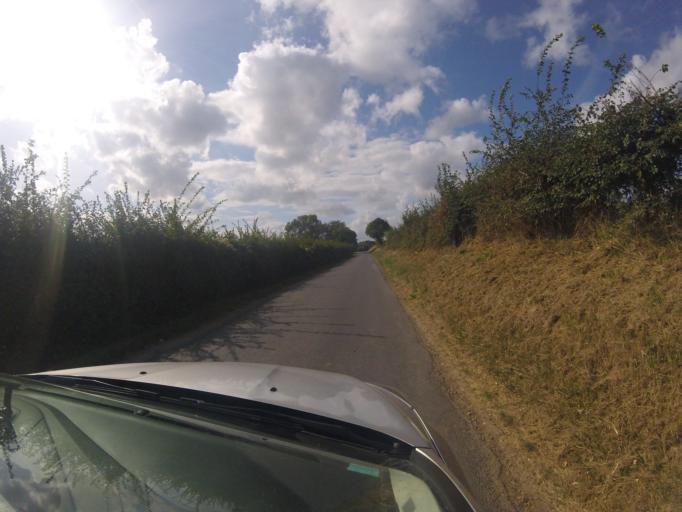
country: FR
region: Lower Normandy
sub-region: Departement du Calvados
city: Saint-Vigor-le-Grand
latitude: 49.3205
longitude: -0.6405
